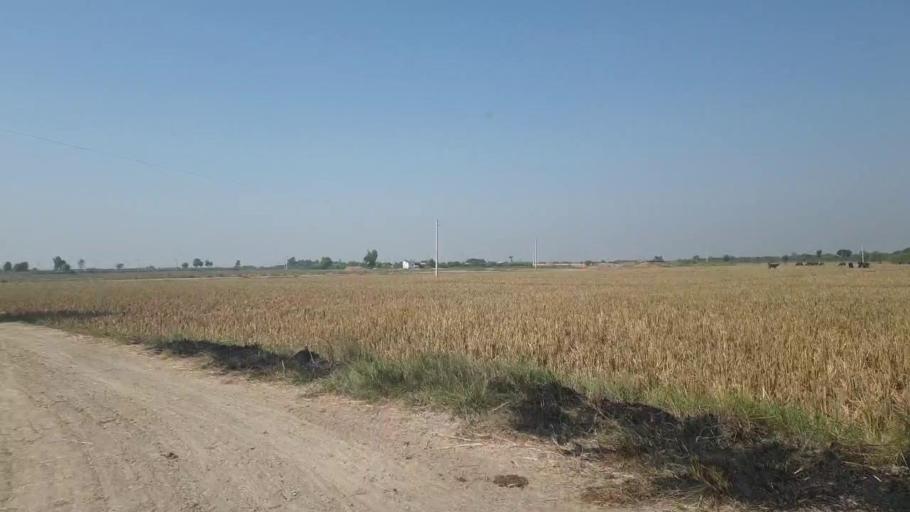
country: PK
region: Sindh
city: Badin
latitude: 24.6931
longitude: 68.8795
